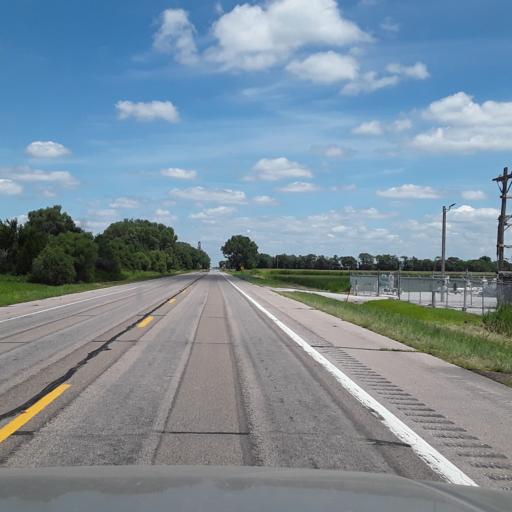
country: US
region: Nebraska
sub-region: Platte County
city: Columbus
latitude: 41.3824
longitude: -97.5073
